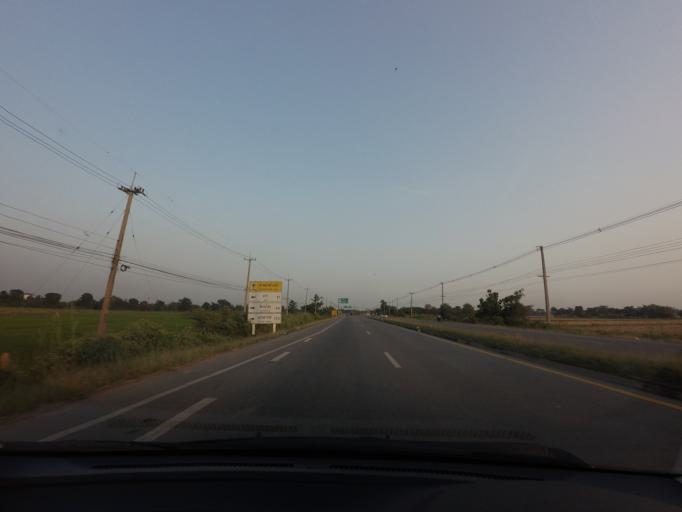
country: TH
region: Sukhothai
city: Kong Krailat
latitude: 17.0093
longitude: 99.9249
